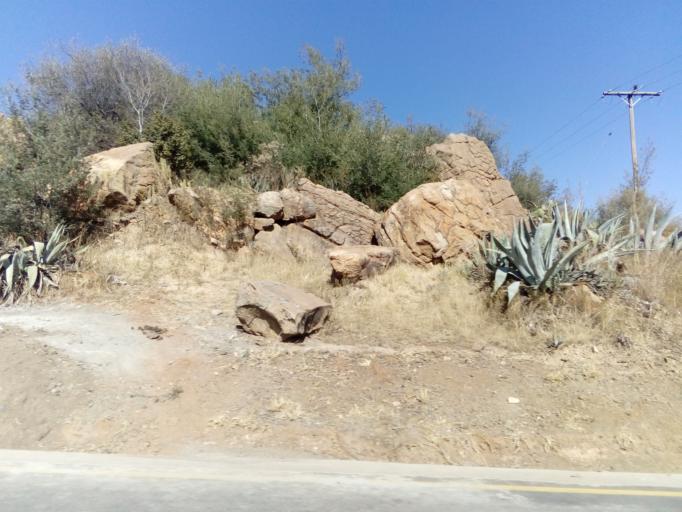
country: LS
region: Berea
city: Teyateyaneng
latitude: -29.1192
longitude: 27.8235
